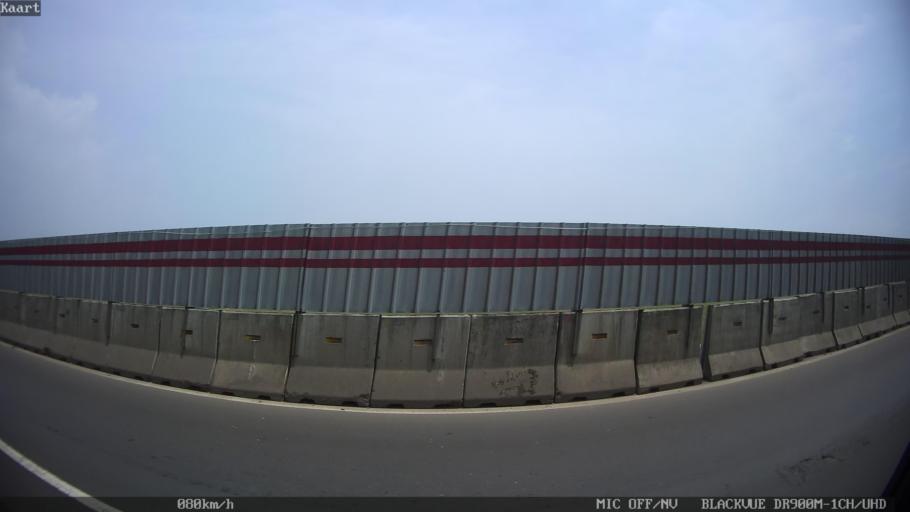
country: ID
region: West Java
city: Kresek
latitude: -6.1492
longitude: 106.3010
